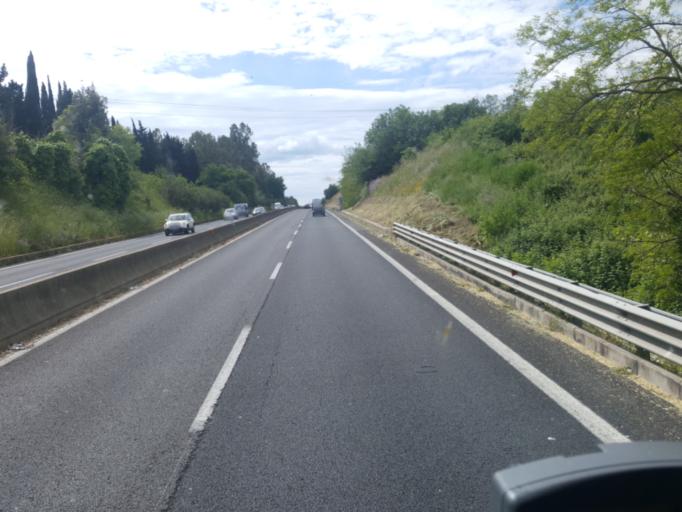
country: IT
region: Latium
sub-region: Citta metropolitana di Roma Capitale
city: La Massimina-Casal Lumbroso
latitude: 41.8860
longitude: 12.3173
